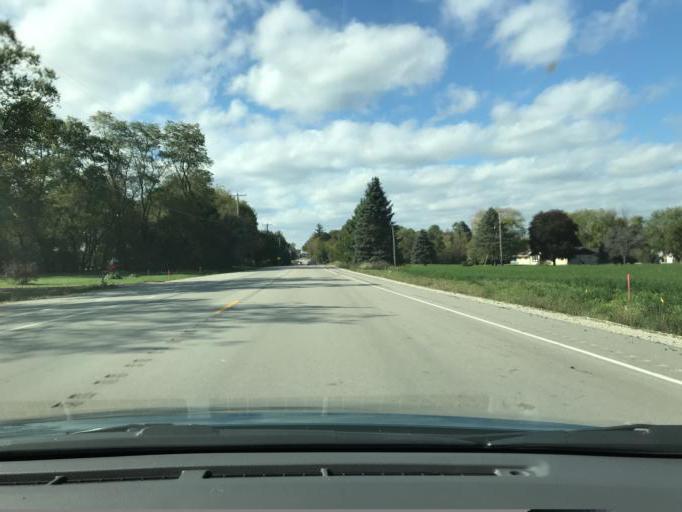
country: US
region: Wisconsin
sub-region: Racine County
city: Browns Lake
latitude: 42.6504
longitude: -88.2065
